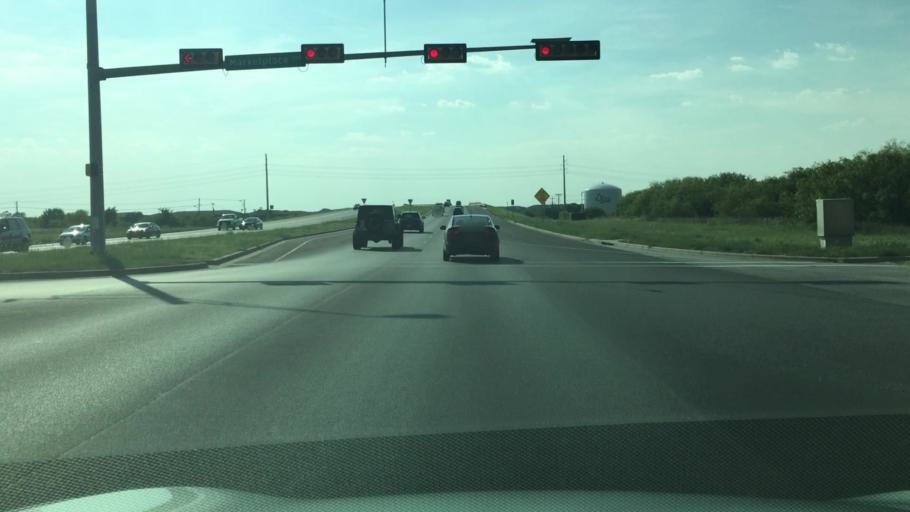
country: US
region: Texas
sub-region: Hays County
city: Kyle
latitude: 30.0155
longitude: -97.8656
